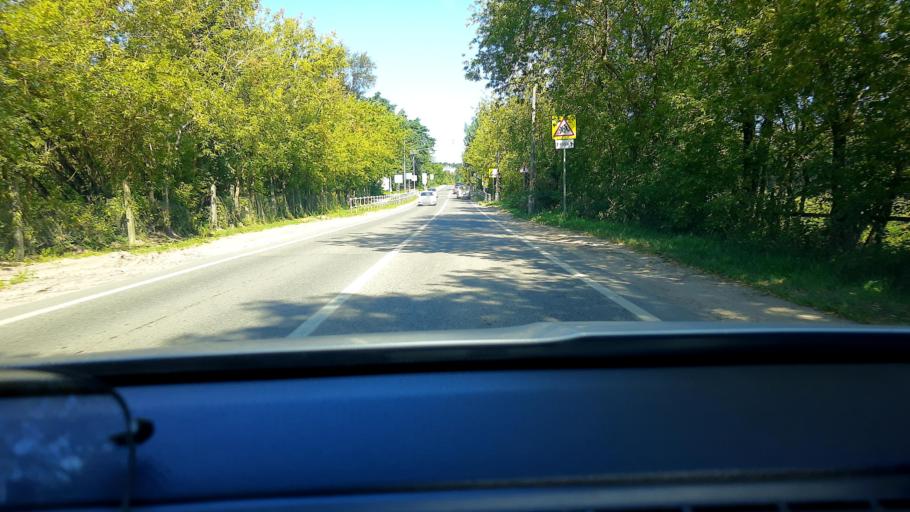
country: RU
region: Moskovskaya
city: Petrovo-Dal'neye
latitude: 55.7639
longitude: 37.2263
